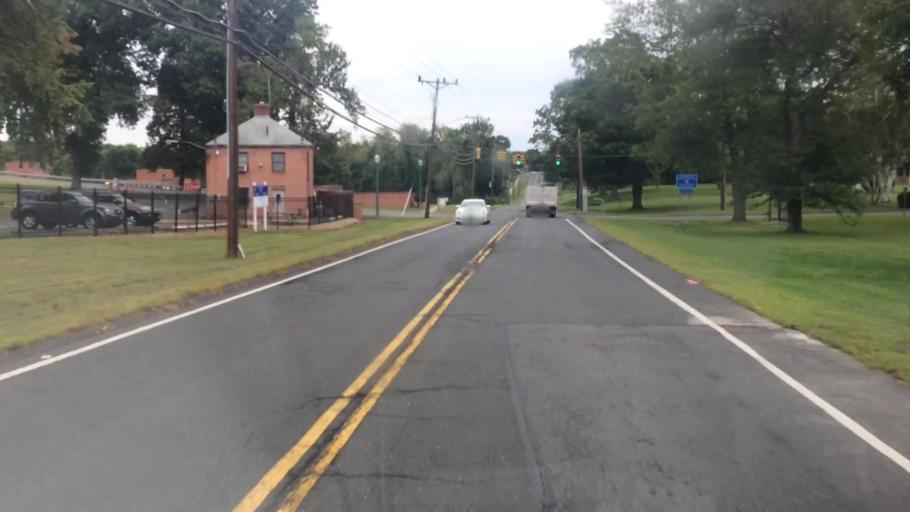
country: US
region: Connecticut
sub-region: Middlesex County
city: Cromwell
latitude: 41.6529
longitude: -72.6541
